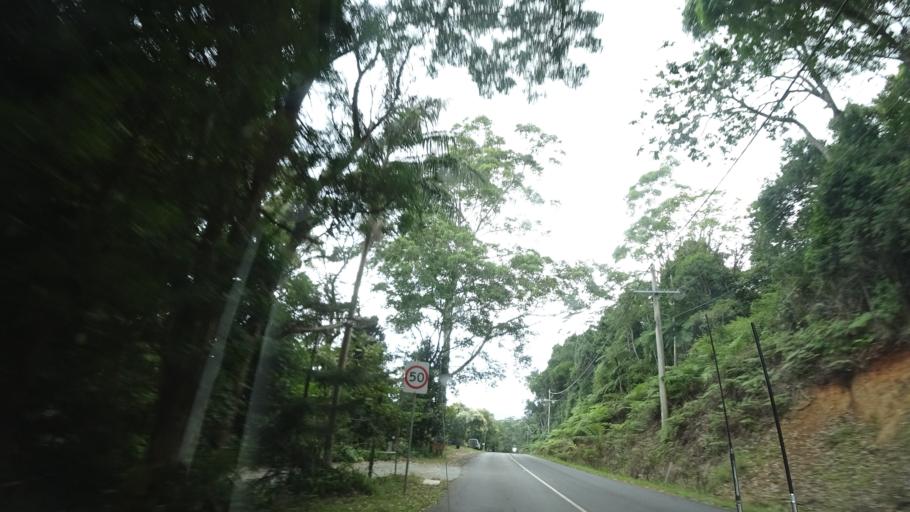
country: AU
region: Queensland
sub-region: Moreton Bay
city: Highvale
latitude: -27.3346
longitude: 152.7707
